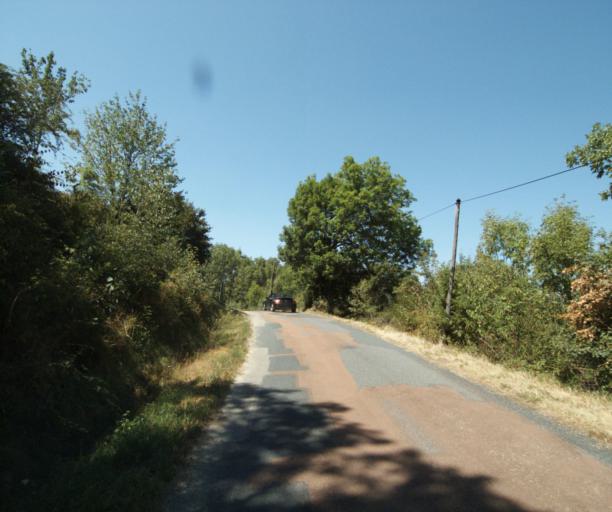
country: FR
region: Rhone-Alpes
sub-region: Departement du Rhone
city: Courzieu
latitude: 45.7485
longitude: 4.5949
